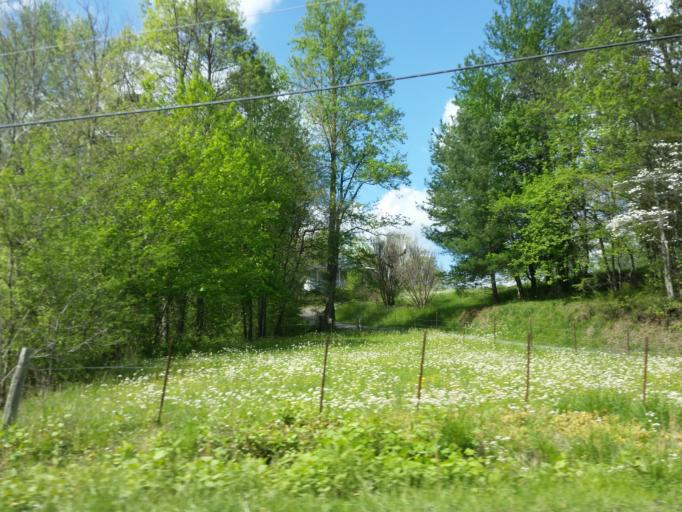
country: US
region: Kentucky
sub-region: Bell County
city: Middlesboro
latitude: 36.6320
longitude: -83.7298
